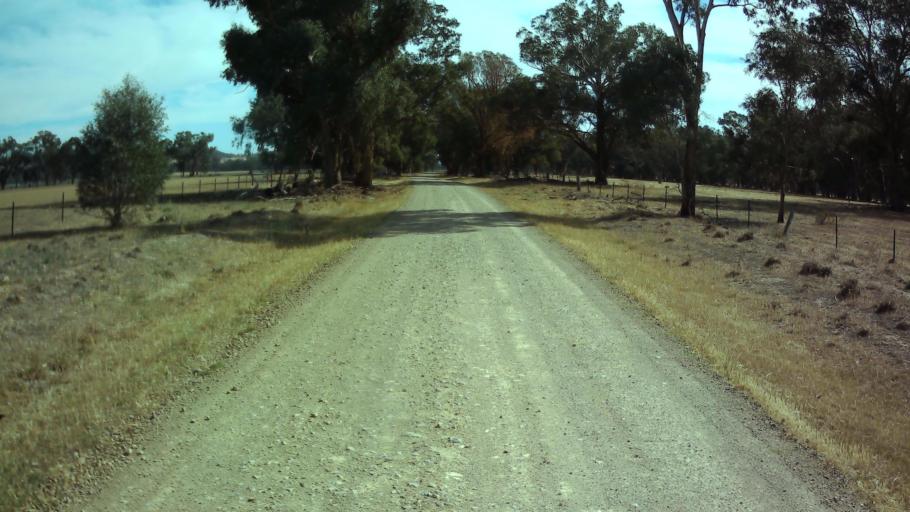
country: AU
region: New South Wales
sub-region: Weddin
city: Grenfell
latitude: -33.6901
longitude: 148.3043
